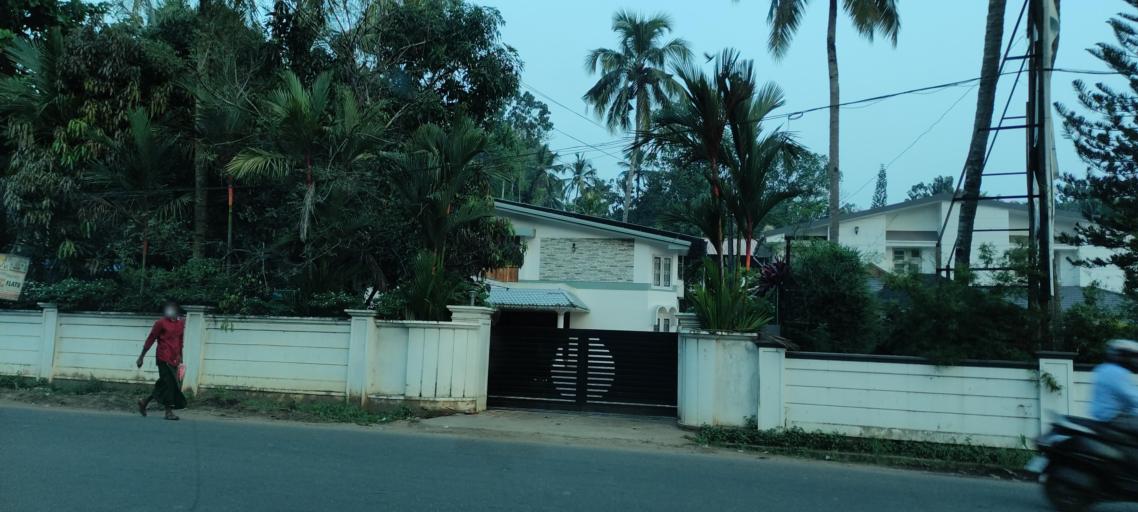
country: IN
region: Kerala
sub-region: Pattanamtitta
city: Adur
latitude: 9.1485
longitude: 76.7332
